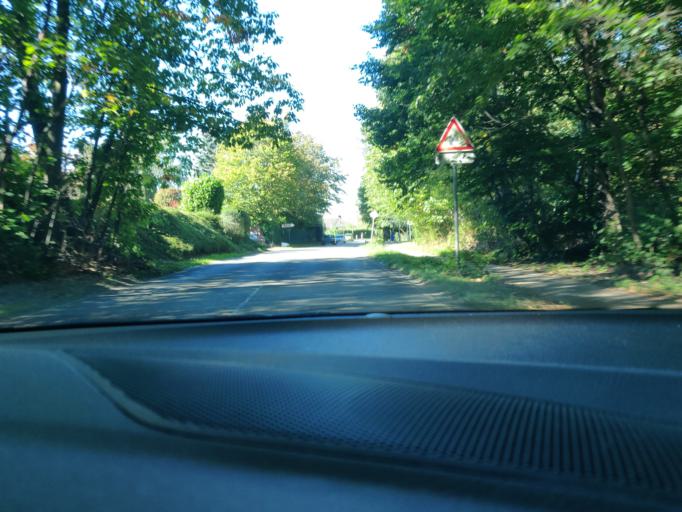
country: DE
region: North Rhine-Westphalia
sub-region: Regierungsbezirk Dusseldorf
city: Heiligenhaus
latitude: 51.3515
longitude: 6.9466
